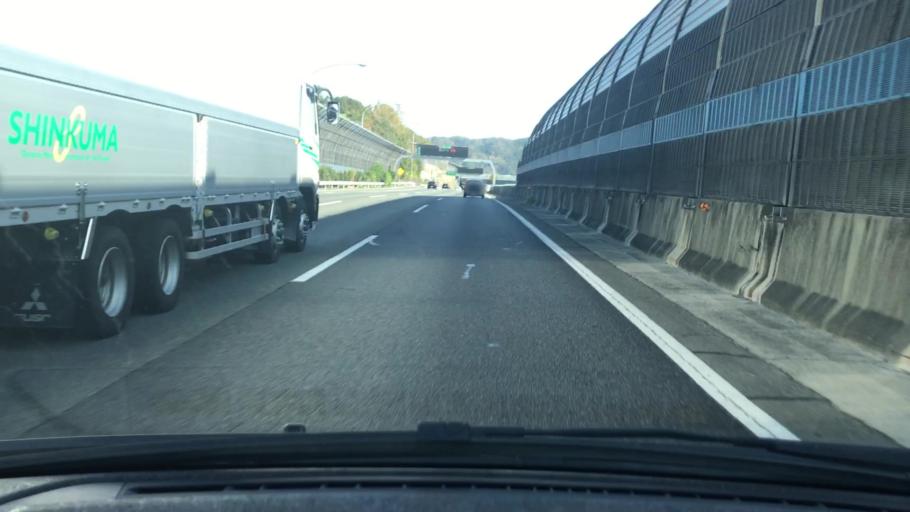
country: JP
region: Osaka
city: Takatsuki
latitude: 34.8652
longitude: 135.6118
